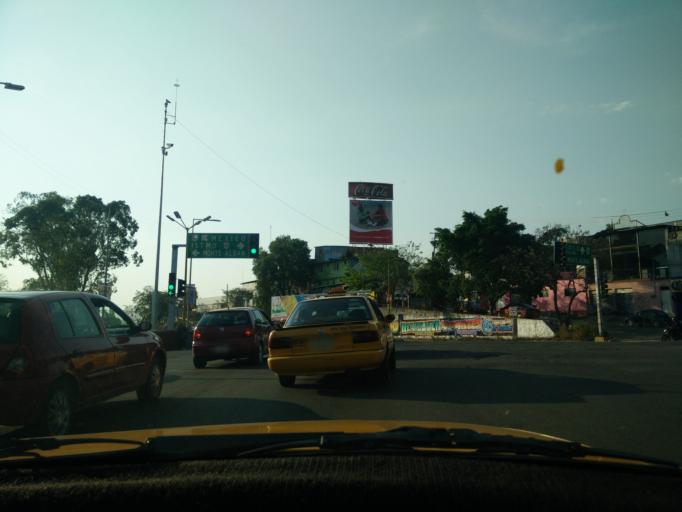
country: MX
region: Oaxaca
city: Oaxaca de Juarez
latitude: 17.0797
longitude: -96.7415
